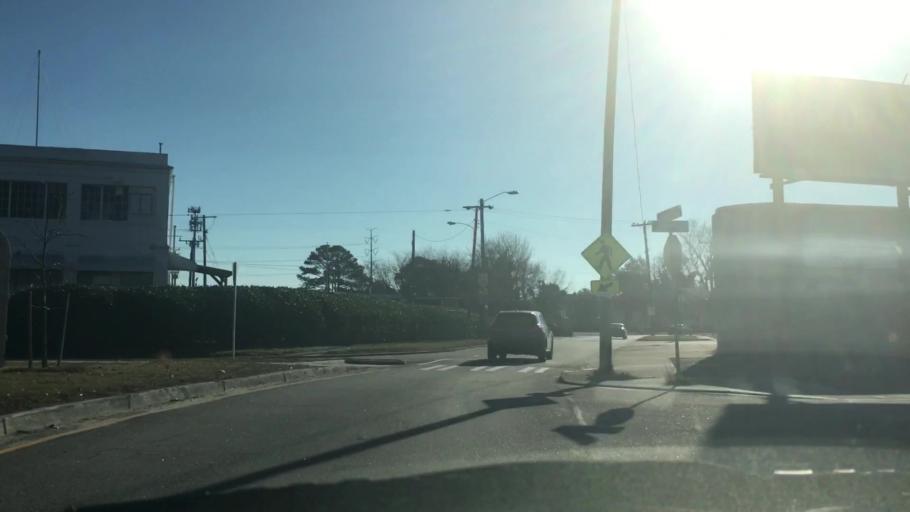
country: US
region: Virginia
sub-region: City of Norfolk
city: Norfolk
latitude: 36.8753
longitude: -76.2542
